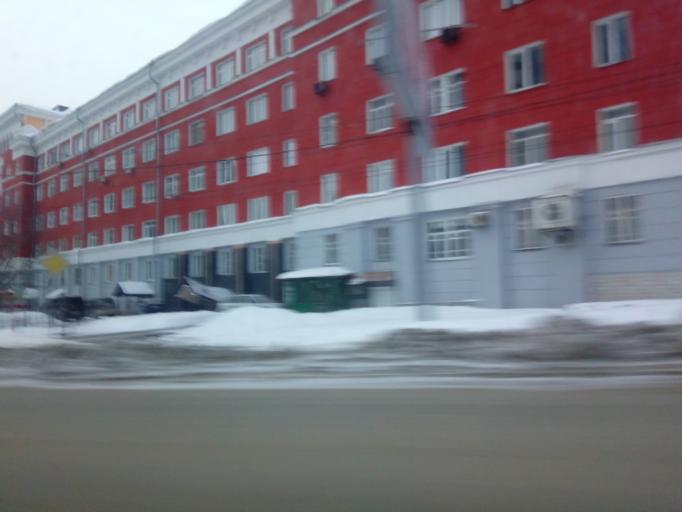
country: RU
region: Novosibirsk
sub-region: Novosibirskiy Rayon
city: Novosibirsk
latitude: 55.0303
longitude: 82.9084
